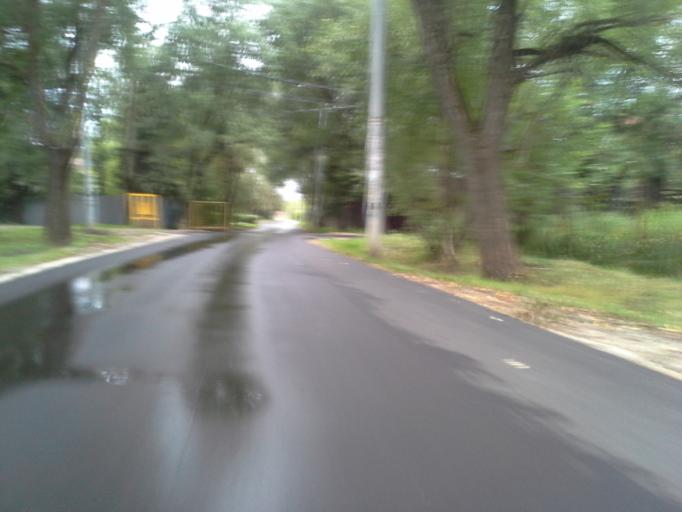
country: RU
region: Moscow
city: Tolstopal'tsevo
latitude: 55.6076
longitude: 37.2128
